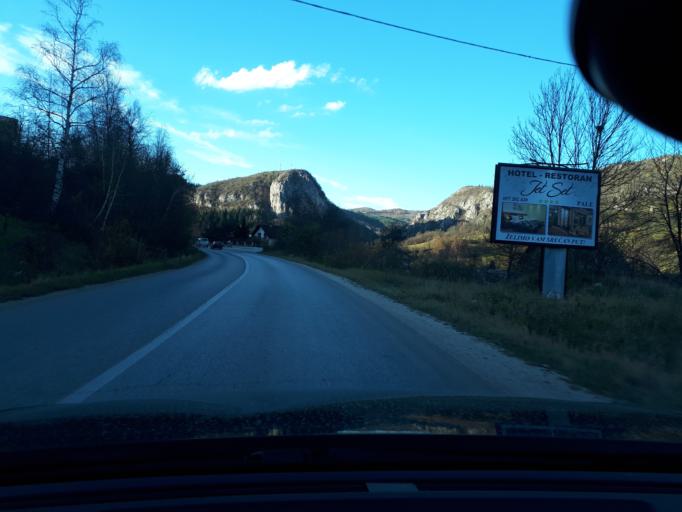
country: BA
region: Republika Srpska
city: Pale
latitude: 43.8460
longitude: 18.5514
